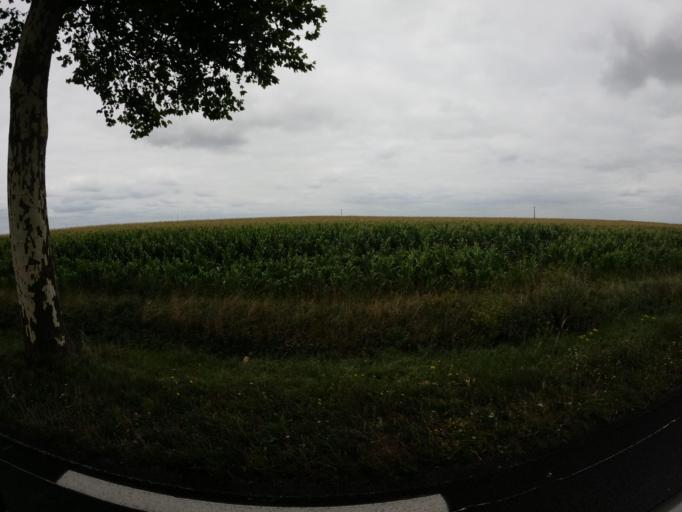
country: FR
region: Pays de la Loire
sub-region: Departement de la Vendee
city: Le Langon
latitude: 46.4997
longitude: -0.9297
